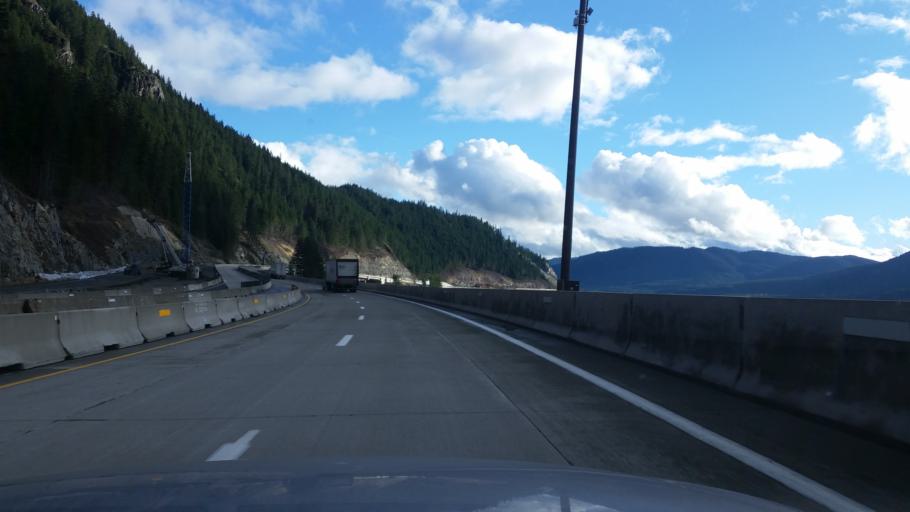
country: US
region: Washington
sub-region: King County
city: Tanner
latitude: 47.3607
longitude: -121.3724
